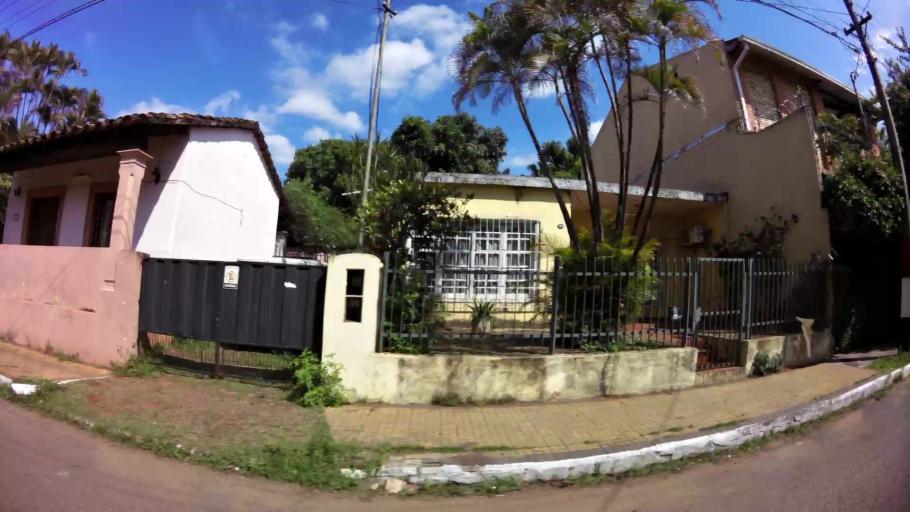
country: PY
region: Central
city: San Lorenzo
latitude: -25.3427
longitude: -57.5127
